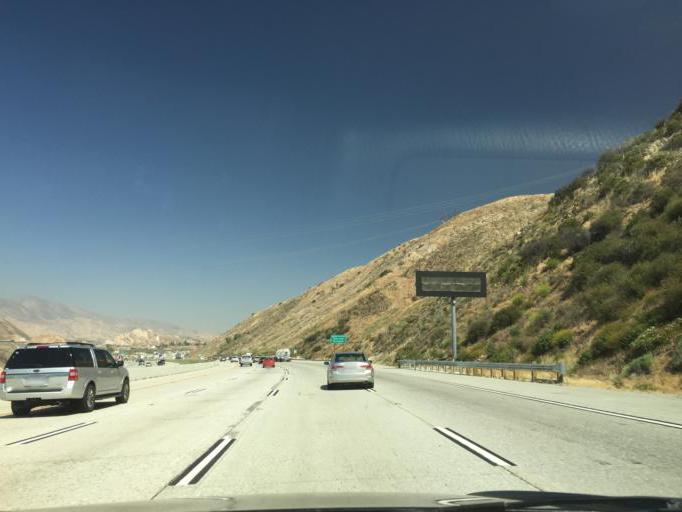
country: US
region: California
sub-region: San Bernardino County
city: Oak Hills
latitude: 34.3024
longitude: -117.4598
